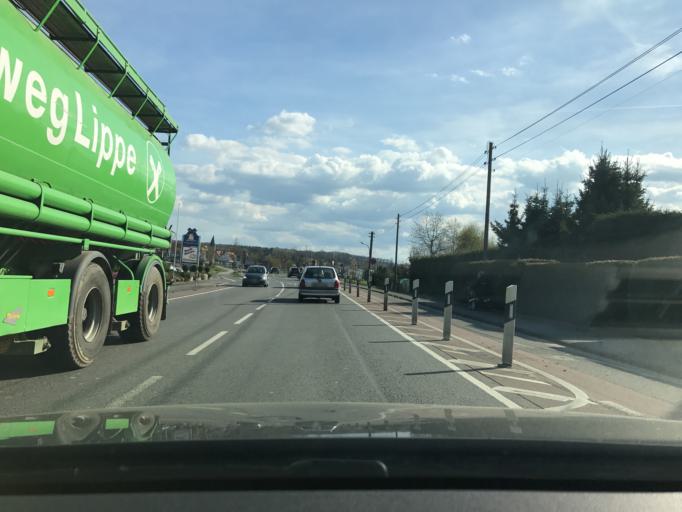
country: DE
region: North Rhine-Westphalia
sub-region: Regierungsbezirk Arnsberg
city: Werl
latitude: 51.5837
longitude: 7.8602
